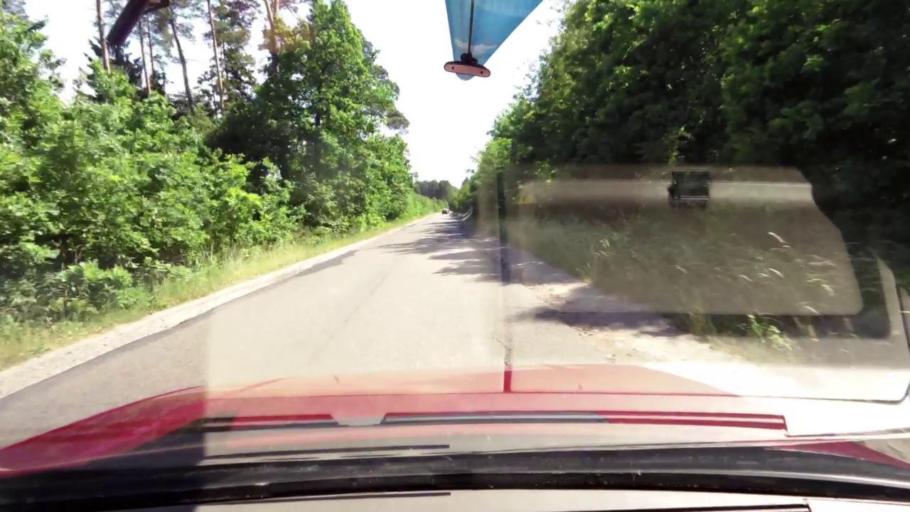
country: PL
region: Pomeranian Voivodeship
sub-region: Powiat slupski
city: Kepice
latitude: 54.3239
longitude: 16.9621
